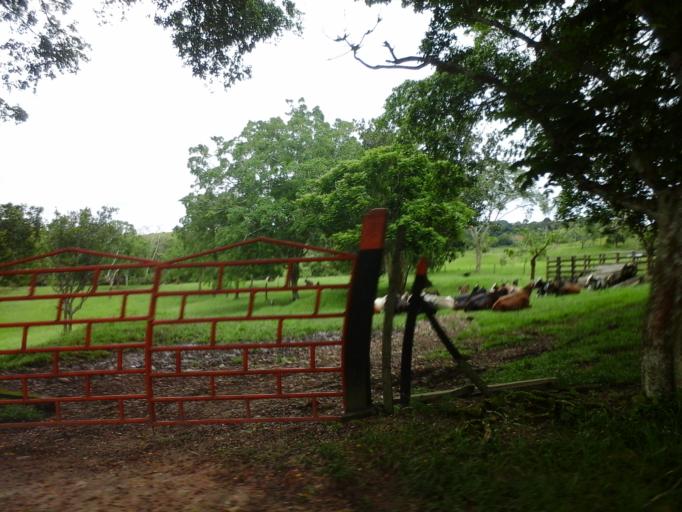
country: CO
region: Caqueta
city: El Doncello
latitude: 1.5967
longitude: -75.0323
